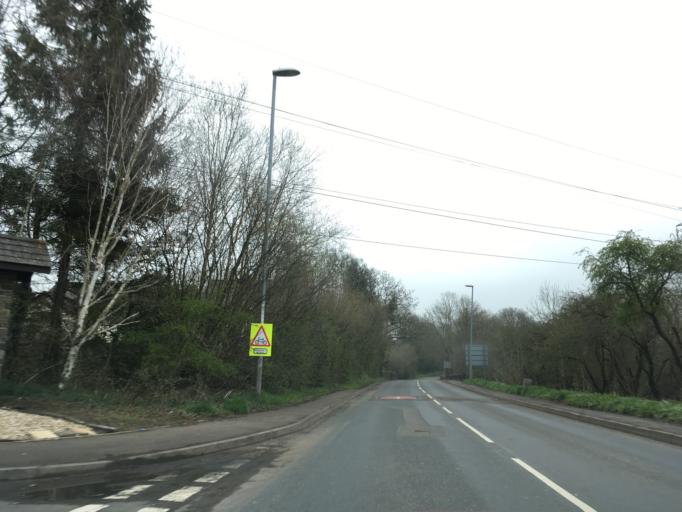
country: GB
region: Wales
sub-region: Newport
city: Caerleon
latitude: 51.6150
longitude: -2.9526
